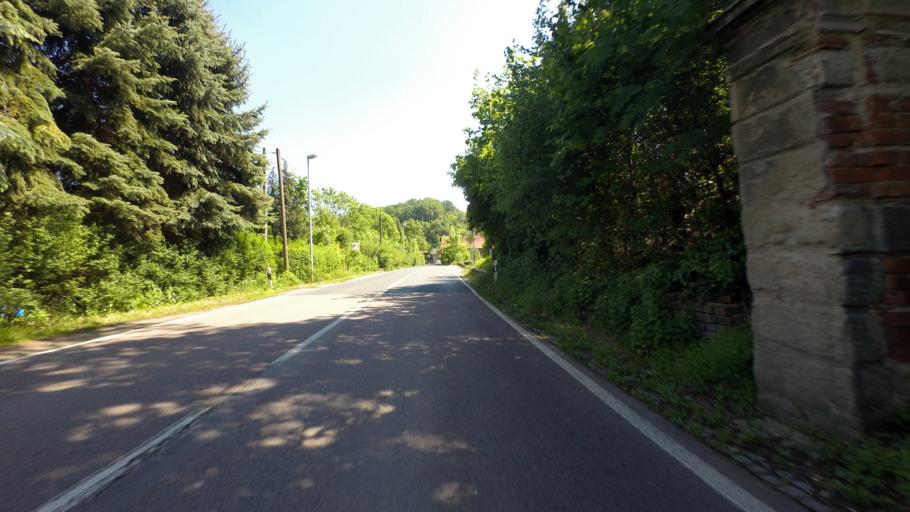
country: DE
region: Saxony
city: Coswig
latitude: 51.1159
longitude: 13.5545
